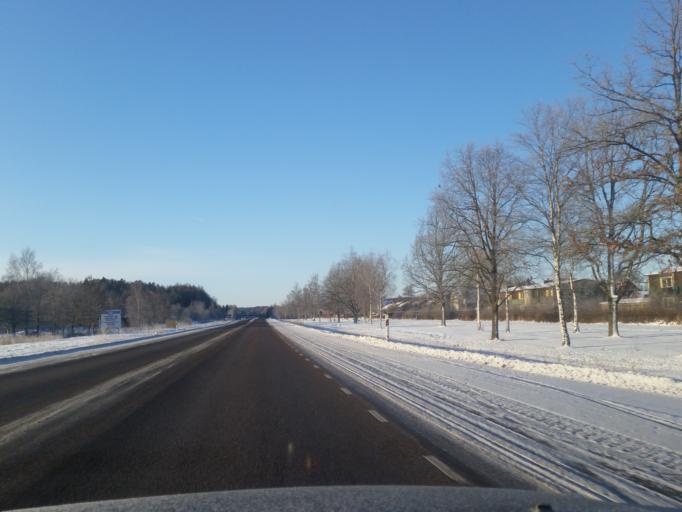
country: SE
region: Vaestmanland
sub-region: Arboga Kommun
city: Arboga
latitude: 59.3927
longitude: 15.8648
